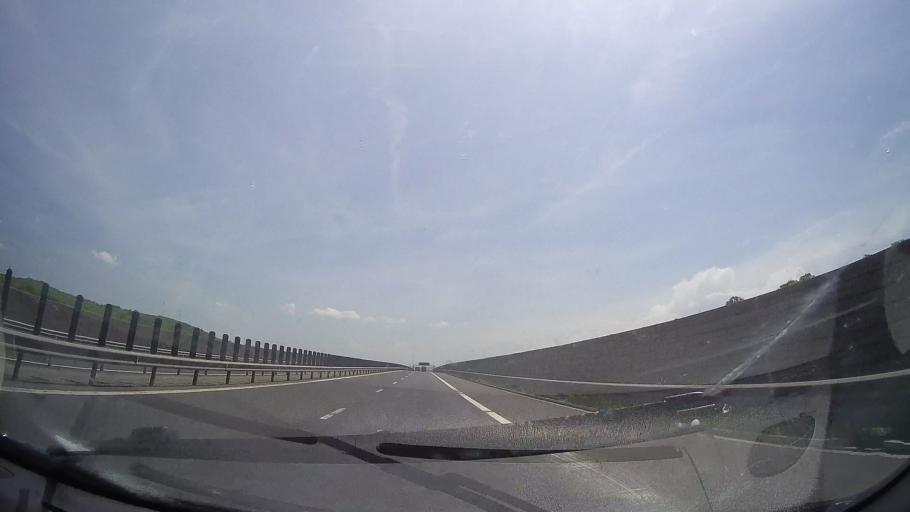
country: RO
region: Alba
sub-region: Comuna Garbova
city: Garbova
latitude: 45.9099
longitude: 23.7408
